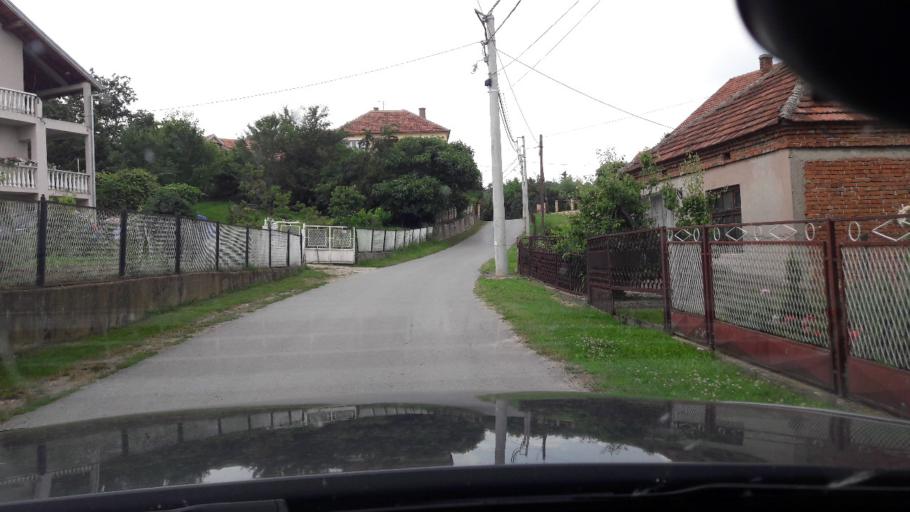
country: RS
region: Central Serbia
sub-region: Belgrade
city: Grocka
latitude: 44.6513
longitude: 20.5985
